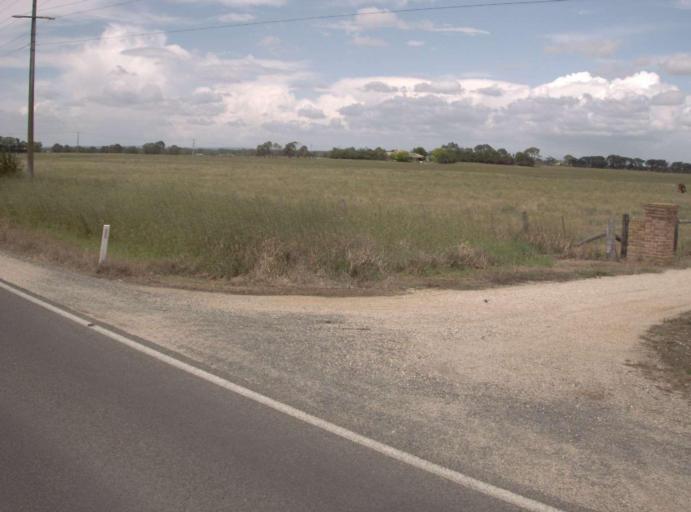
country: AU
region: Victoria
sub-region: Wellington
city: Sale
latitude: -38.0196
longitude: 147.0103
